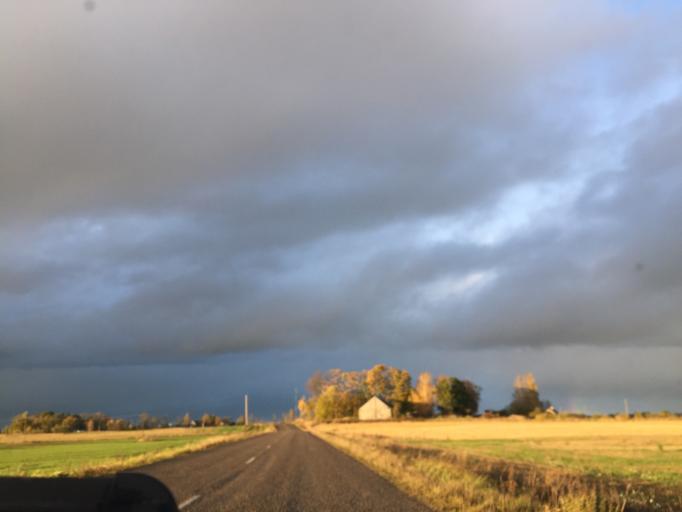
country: LV
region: Talsu Rajons
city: Sabile
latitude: 56.9331
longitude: 22.3973
